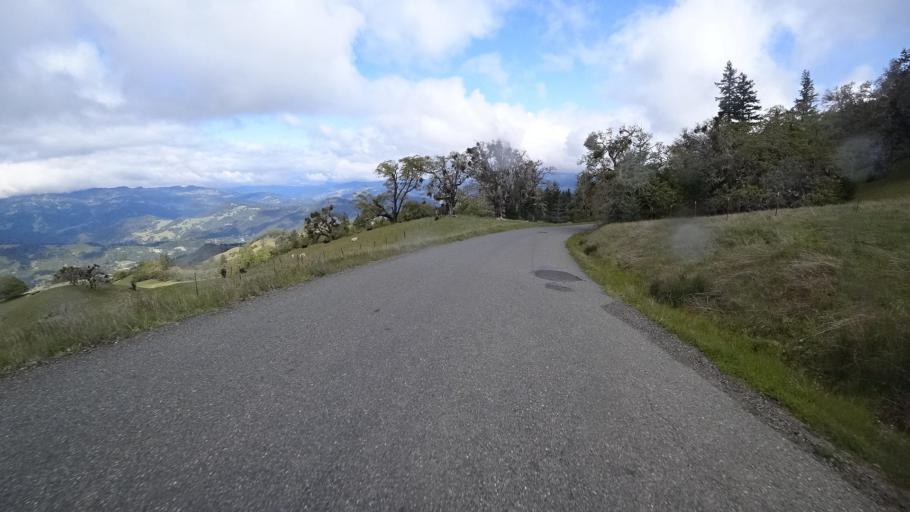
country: US
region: California
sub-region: Humboldt County
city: Redway
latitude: 40.1551
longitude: -123.5588
